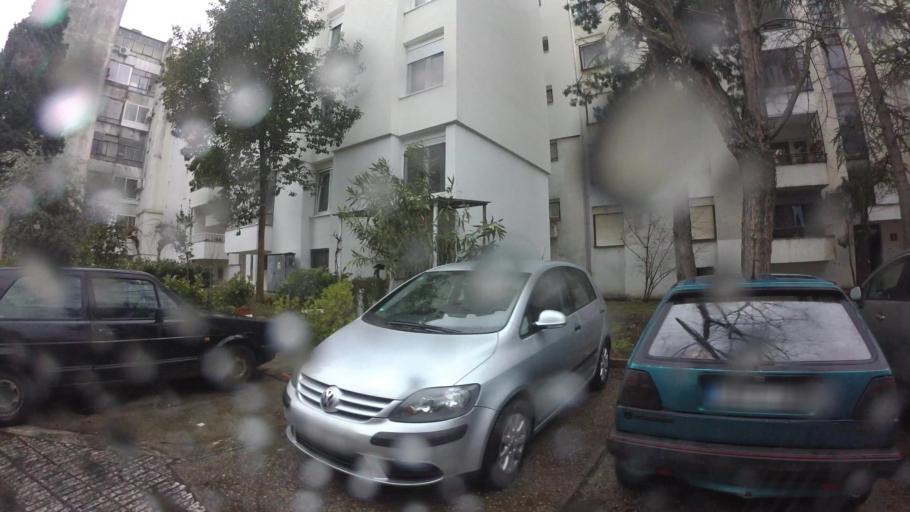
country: BA
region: Federation of Bosnia and Herzegovina
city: Cim
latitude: 43.3469
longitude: 17.7935
